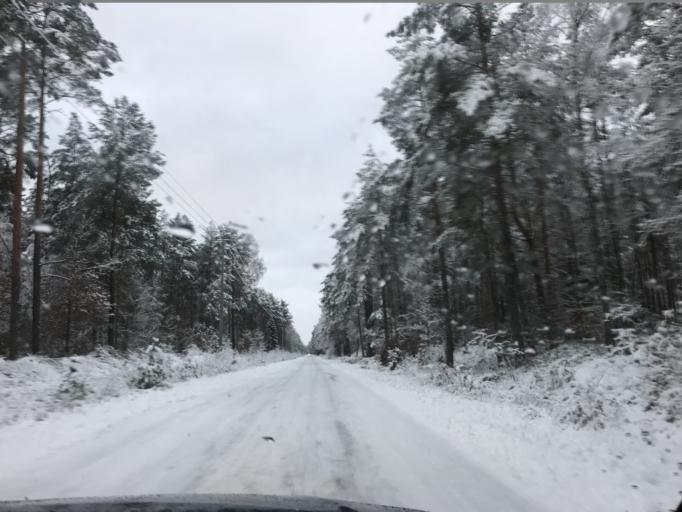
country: PL
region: Pomeranian Voivodeship
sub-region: Powiat bytowski
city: Czarna Dabrowka
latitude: 54.2862
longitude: 17.6001
